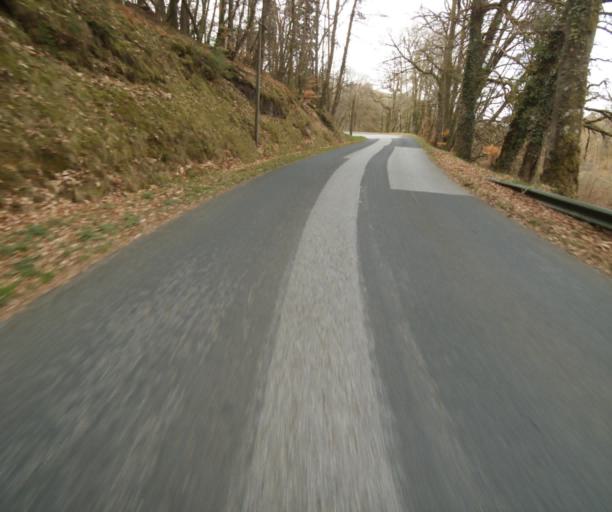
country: FR
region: Limousin
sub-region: Departement de la Correze
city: Treignac
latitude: 45.4465
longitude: 1.8054
